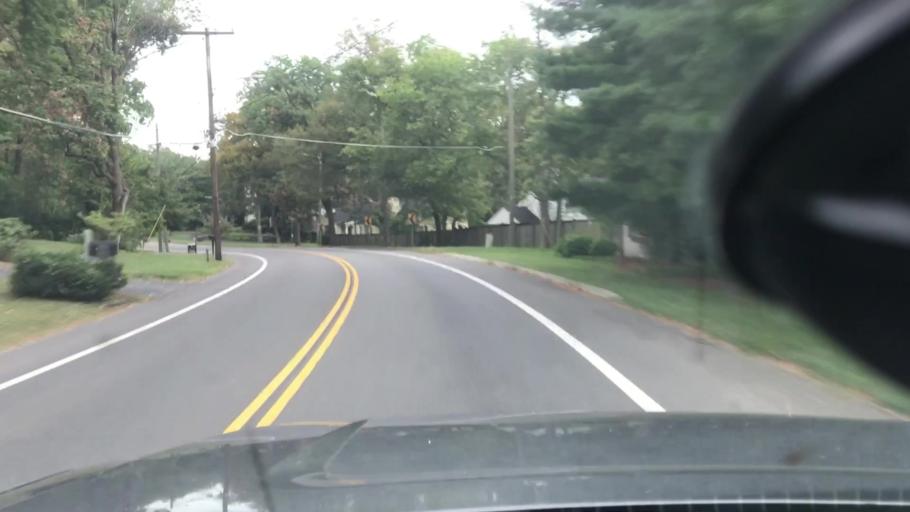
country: US
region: Tennessee
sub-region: Davidson County
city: Belle Meade
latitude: 36.1172
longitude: -86.8404
